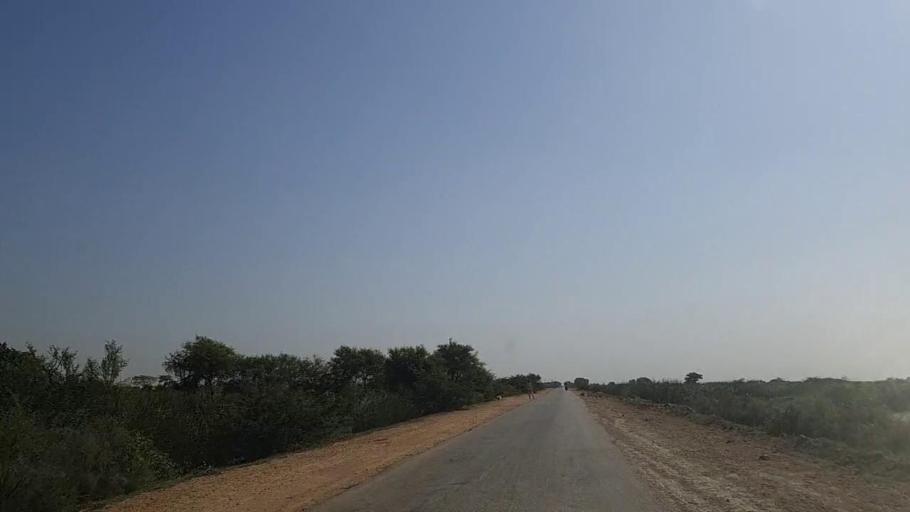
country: PK
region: Sindh
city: Mirpur Batoro
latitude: 24.6474
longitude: 68.2892
